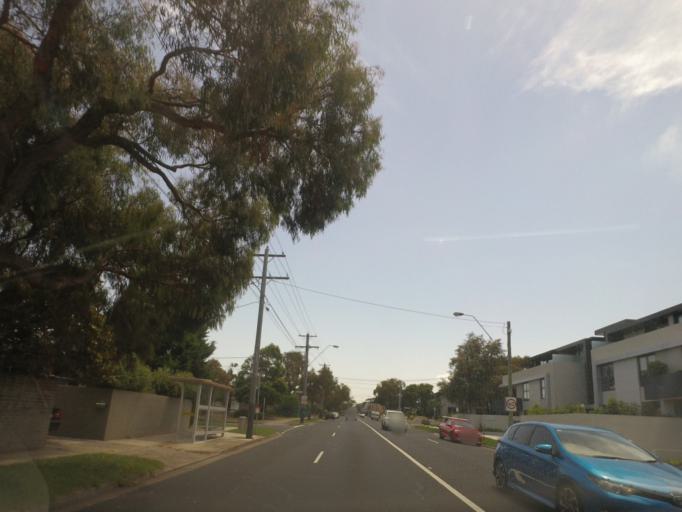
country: AU
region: Victoria
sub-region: Bayside
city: Black Rock
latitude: -37.9729
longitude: 145.0166
